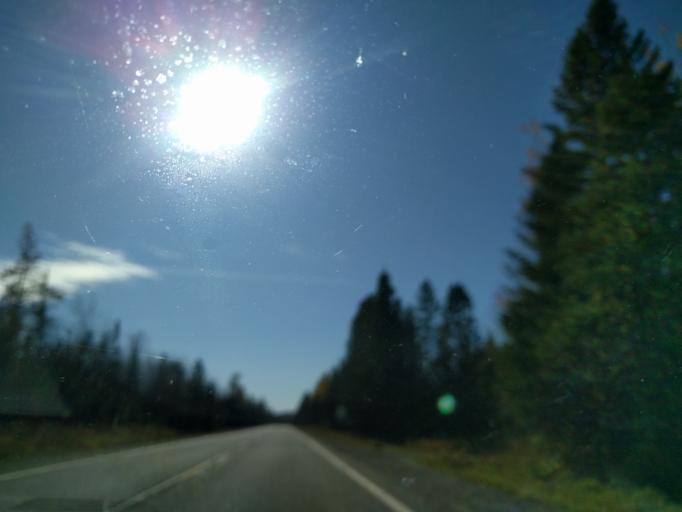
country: US
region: Michigan
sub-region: Marquette County
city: West Ishpeming
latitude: 46.4693
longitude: -87.9300
